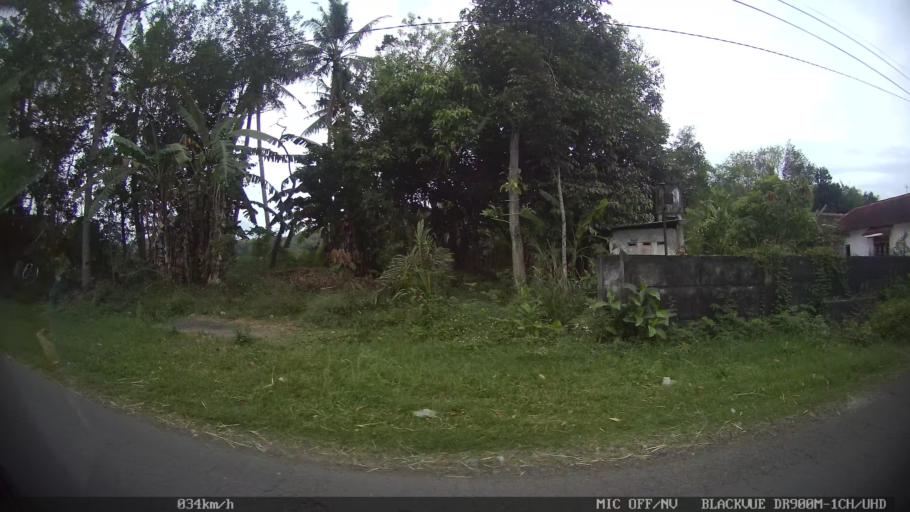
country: ID
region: Daerah Istimewa Yogyakarta
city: Sewon
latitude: -7.8769
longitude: 110.4171
